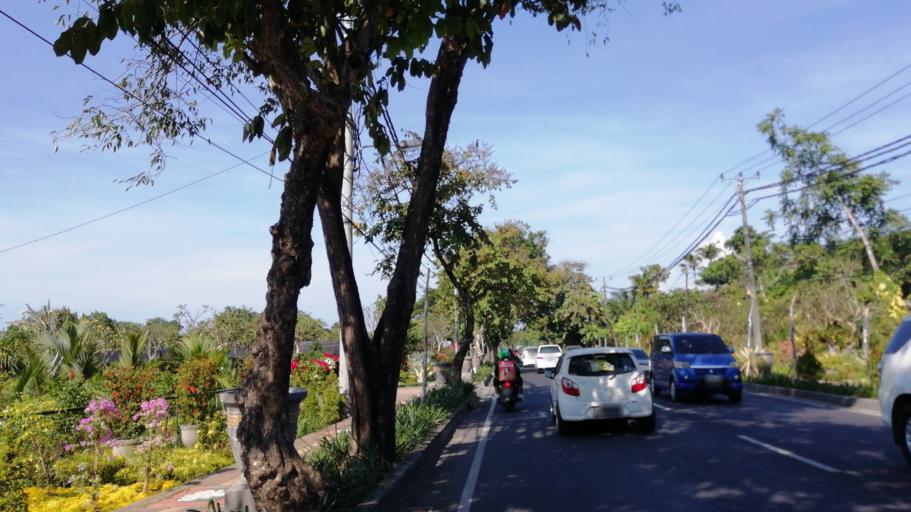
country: ID
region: Bali
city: Banjar Batanpoh
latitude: -8.6737
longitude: 115.2475
